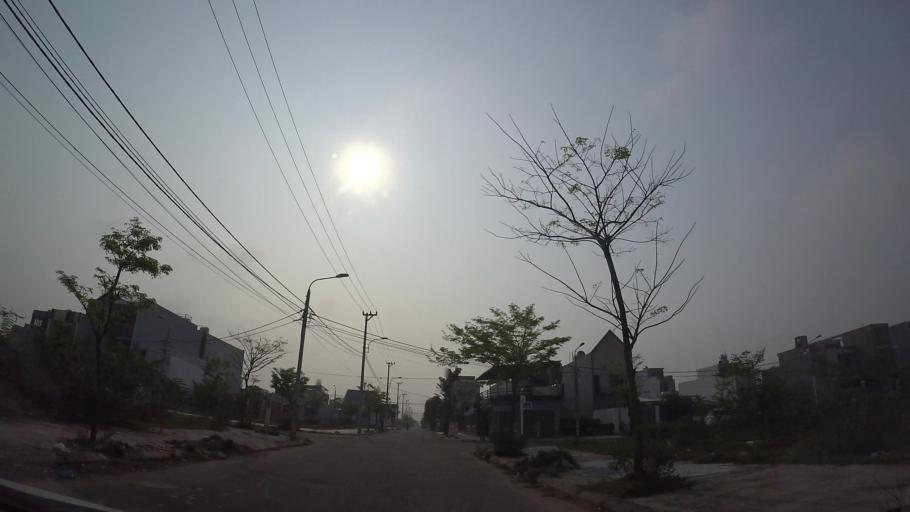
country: VN
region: Da Nang
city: Cam Le
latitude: 16.0093
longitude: 108.2255
